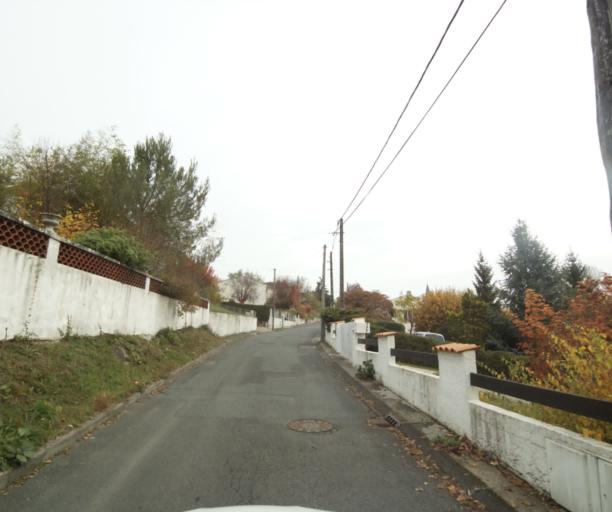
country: FR
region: Poitou-Charentes
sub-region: Departement de la Charente-Maritime
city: Saintes
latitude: 45.7426
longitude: -0.6479
